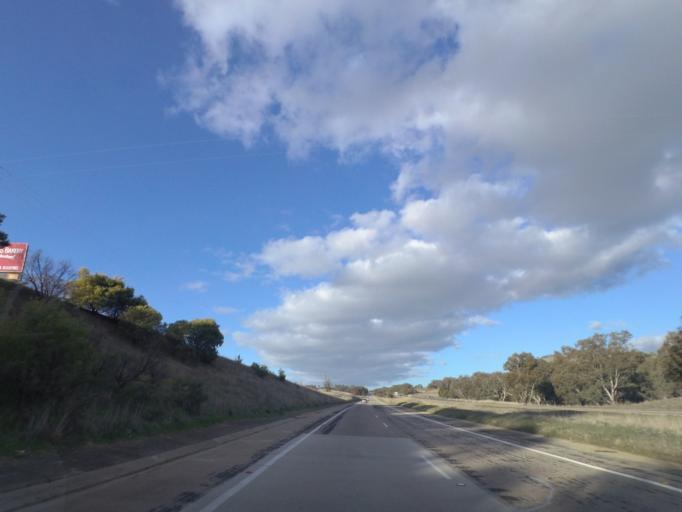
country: AU
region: New South Wales
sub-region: Yass Valley
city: Yass
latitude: -34.8066
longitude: 148.4699
